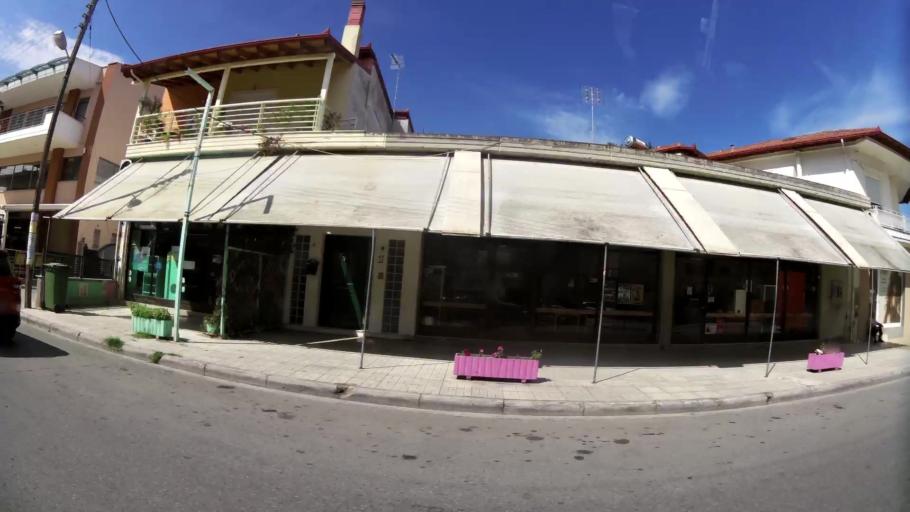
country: GR
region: Central Macedonia
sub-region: Nomos Pierias
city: Katerini
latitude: 40.2792
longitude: 22.5039
